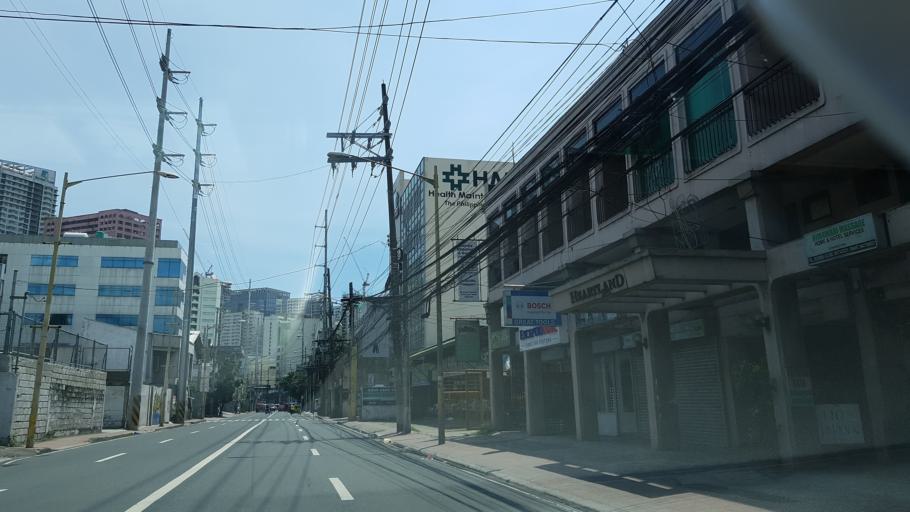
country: PH
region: Metro Manila
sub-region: Makati City
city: Makati City
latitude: 14.5654
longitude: 121.0122
